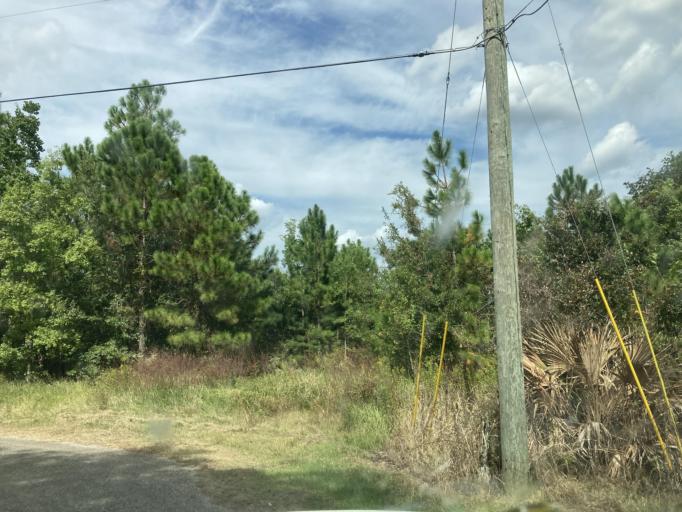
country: US
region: Mississippi
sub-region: Jackson County
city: Saint Martin
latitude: 30.4325
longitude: -88.8755
